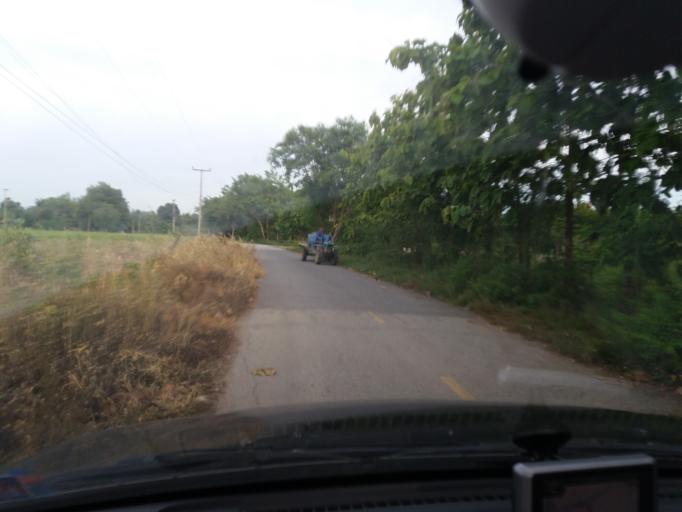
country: TH
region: Suphan Buri
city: Doembang Nangbuat
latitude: 14.8103
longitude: 100.1435
